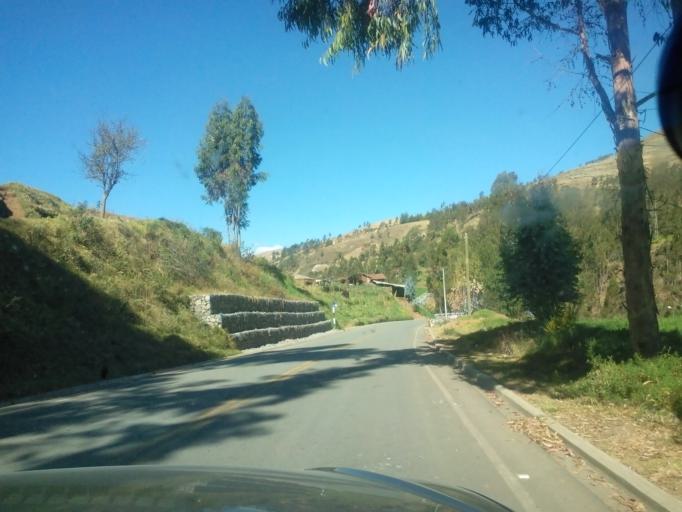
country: PE
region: Apurimac
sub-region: Provincia de Andahuaylas
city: Talavera
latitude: -13.6522
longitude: -73.5138
